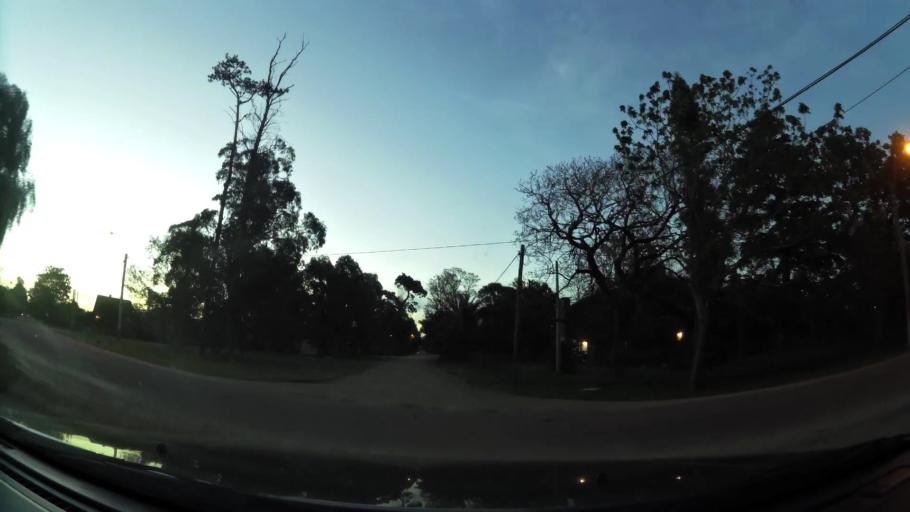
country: UY
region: Canelones
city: Atlantida
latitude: -34.7677
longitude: -55.7564
